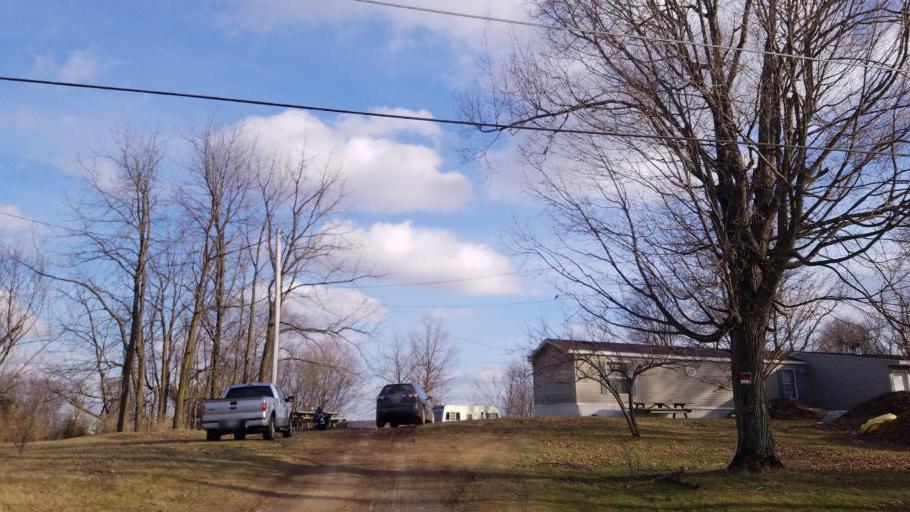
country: US
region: Ohio
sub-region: Crawford County
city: Galion
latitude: 40.7070
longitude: -82.7168
